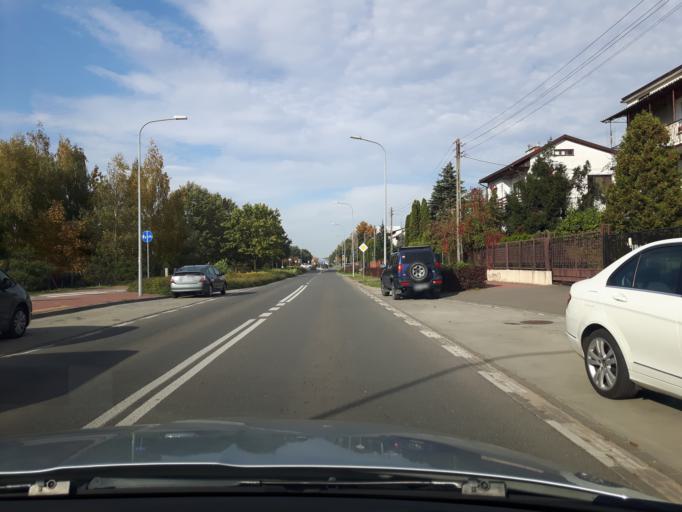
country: PL
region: Masovian Voivodeship
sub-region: Powiat wolominski
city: Zabki
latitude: 52.2952
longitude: 21.0973
